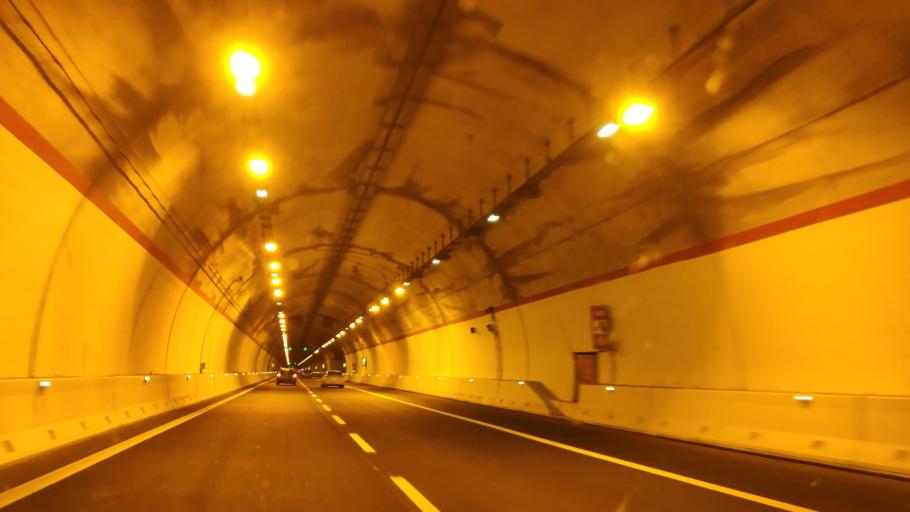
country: IT
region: Campania
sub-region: Provincia di Salerno
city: Casalbuono
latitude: 40.2022
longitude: 15.6853
